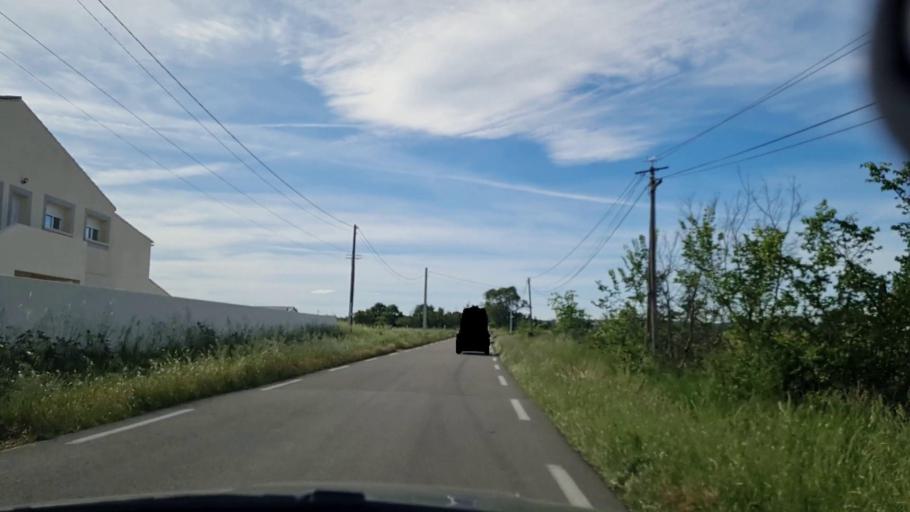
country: FR
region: Languedoc-Roussillon
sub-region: Departement du Gard
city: Saint-Mamert-du-Gard
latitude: 43.9029
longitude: 4.2152
